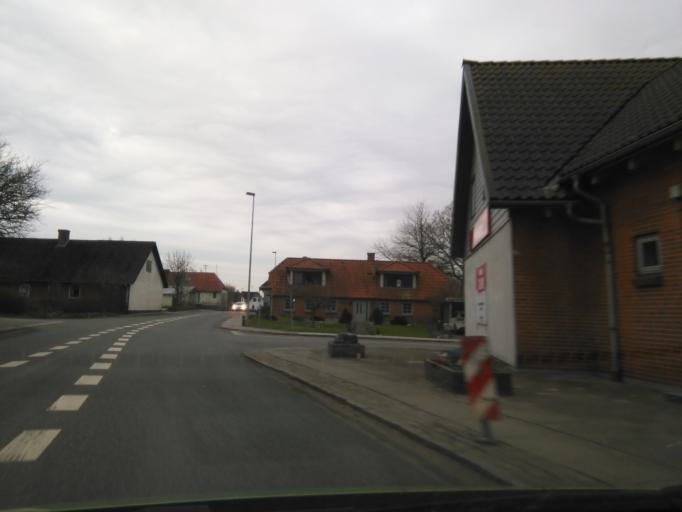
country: DK
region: Central Jutland
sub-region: Randers Kommune
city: Spentrup
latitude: 56.5752
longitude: 9.9961
